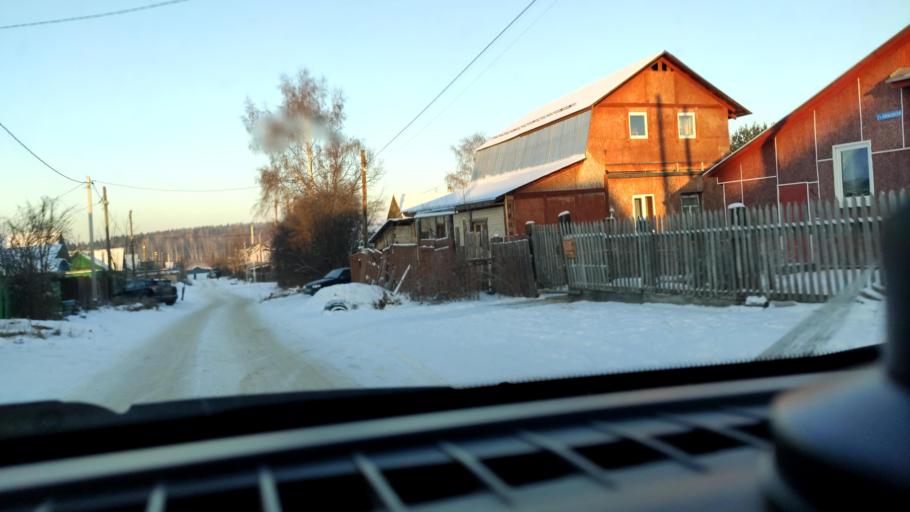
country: RU
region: Perm
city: Kondratovo
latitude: 58.0470
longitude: 56.0523
